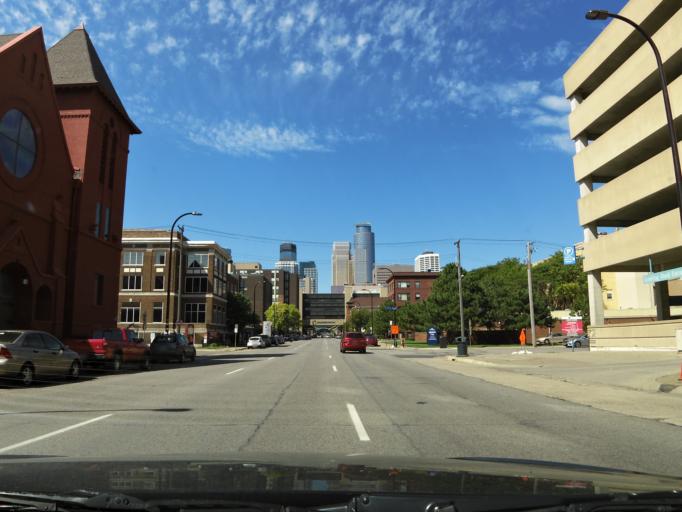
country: US
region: Minnesota
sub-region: Hennepin County
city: Minneapolis
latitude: 44.9709
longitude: -93.2581
